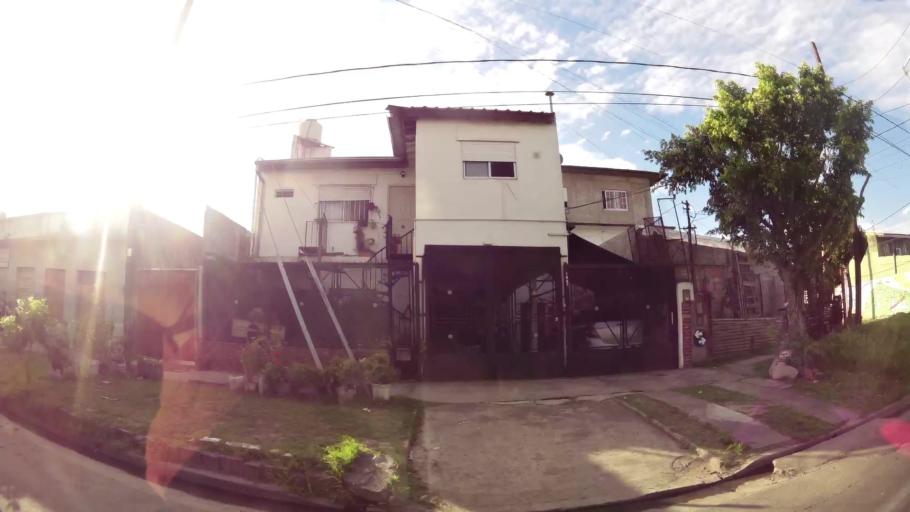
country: AR
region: Buenos Aires
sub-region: Partido de Lanus
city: Lanus
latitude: -34.7089
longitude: -58.3496
